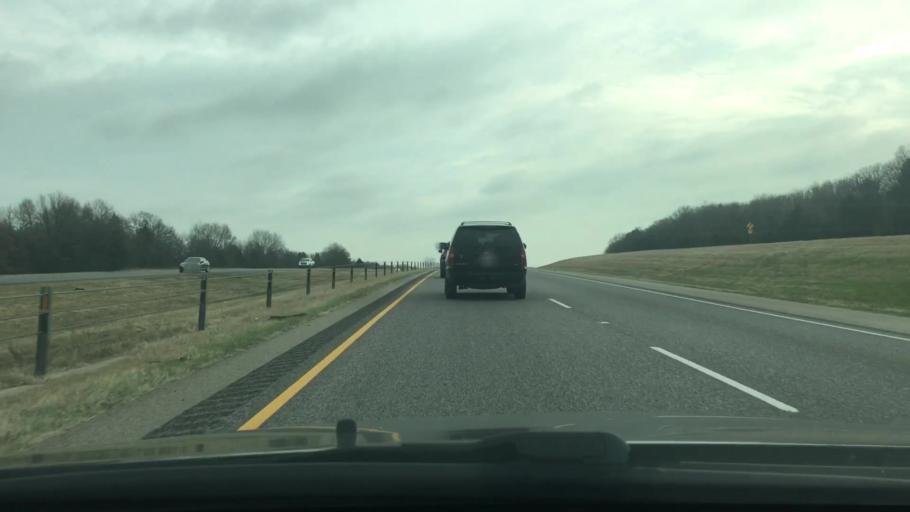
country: US
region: Texas
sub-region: Freestone County
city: Fairfield
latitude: 31.6417
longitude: -96.1588
